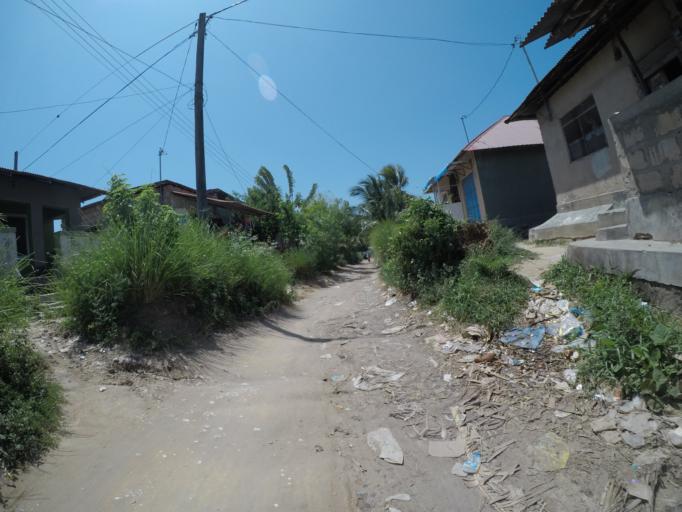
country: TZ
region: Zanzibar Urban/West
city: Zanzibar
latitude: -6.1785
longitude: 39.2065
